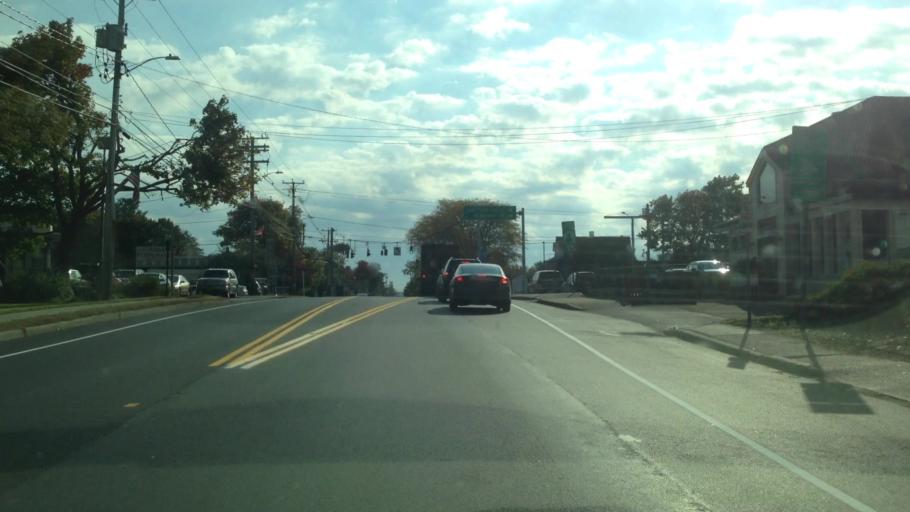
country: US
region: New York
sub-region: Ulster County
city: New Paltz
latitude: 41.7464
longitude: -74.0791
